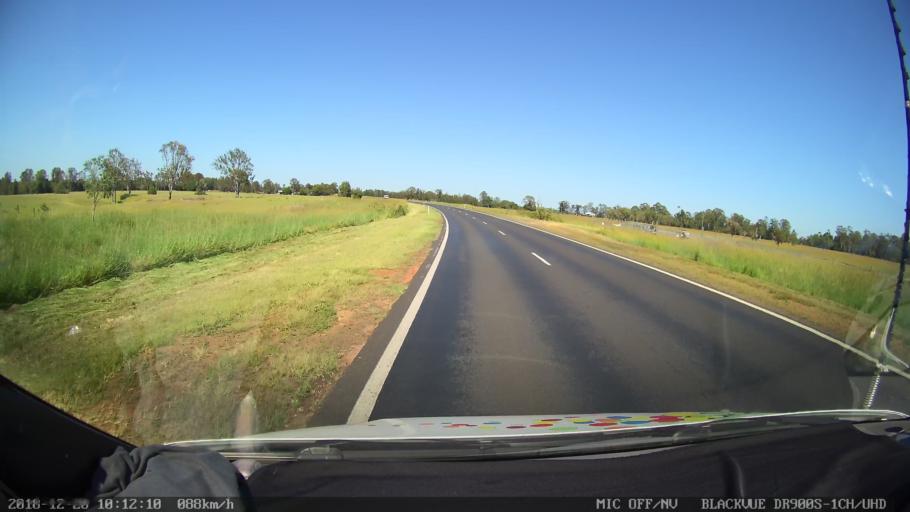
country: AU
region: New South Wales
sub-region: Richmond Valley
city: Casino
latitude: -28.8717
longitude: 153.1476
